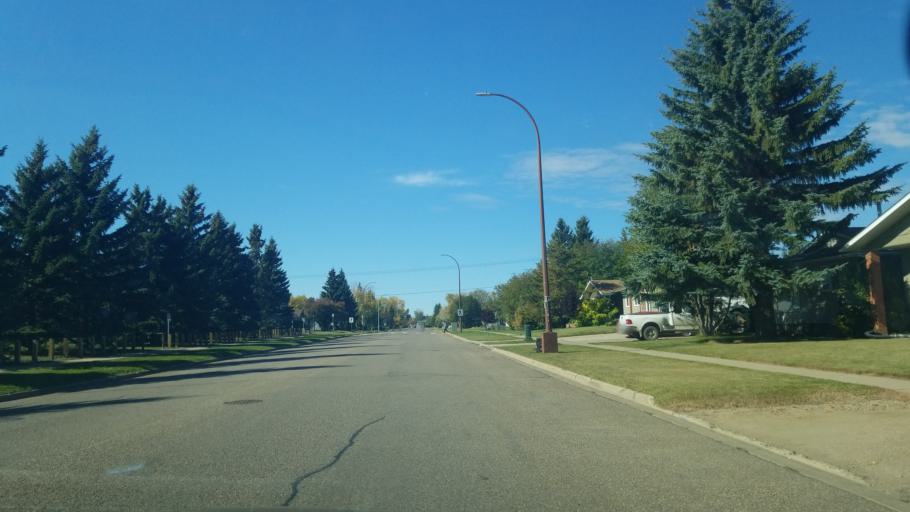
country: CA
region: Saskatchewan
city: Lloydminster
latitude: 53.2730
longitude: -110.0162
